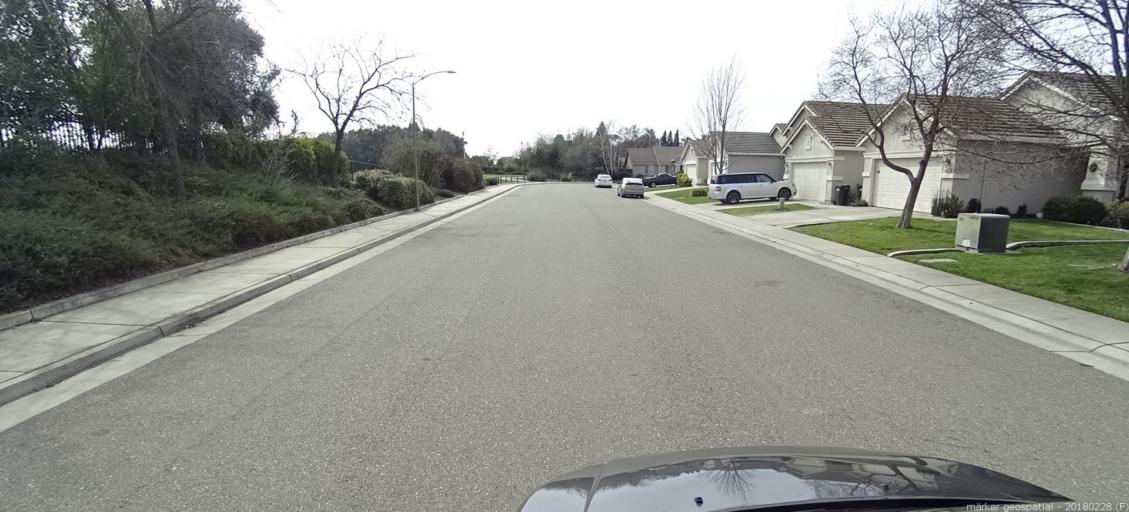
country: US
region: California
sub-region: Sacramento County
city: Antelope
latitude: 38.7193
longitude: -121.3293
